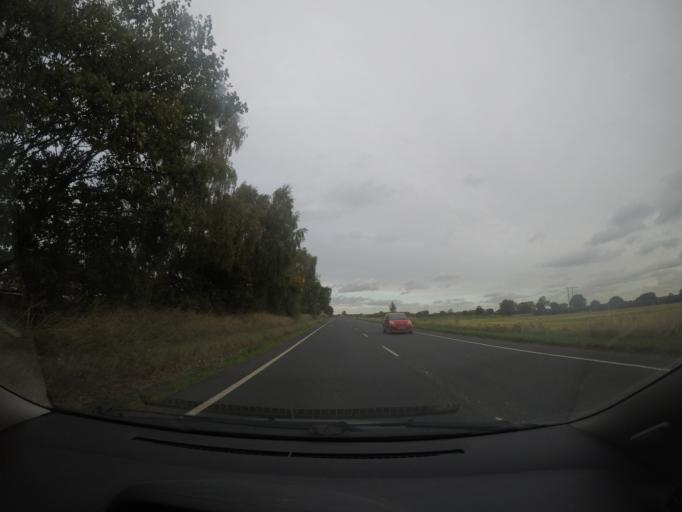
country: GB
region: England
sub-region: North Yorkshire
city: Barlby
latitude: 53.8021
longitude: -1.0360
